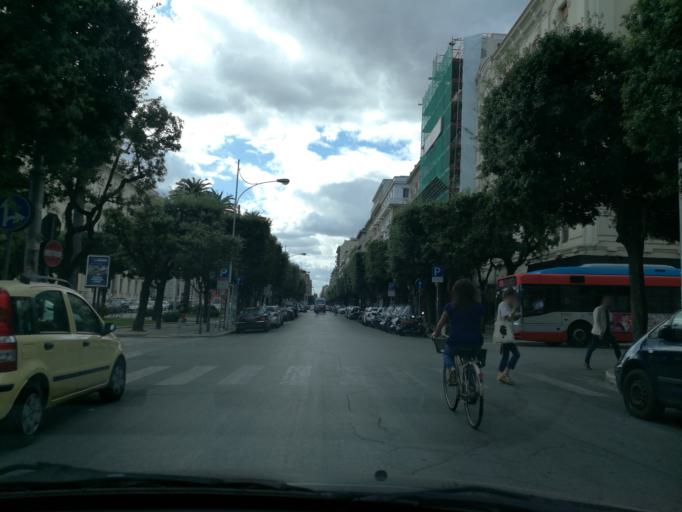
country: IT
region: Apulia
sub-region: Provincia di Bari
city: Bari
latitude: 41.1257
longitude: 16.8721
